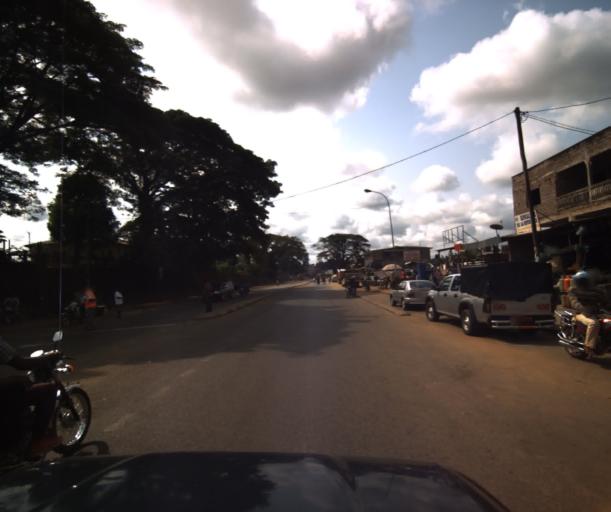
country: CM
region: Littoral
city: Edea
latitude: 3.7961
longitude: 10.1309
